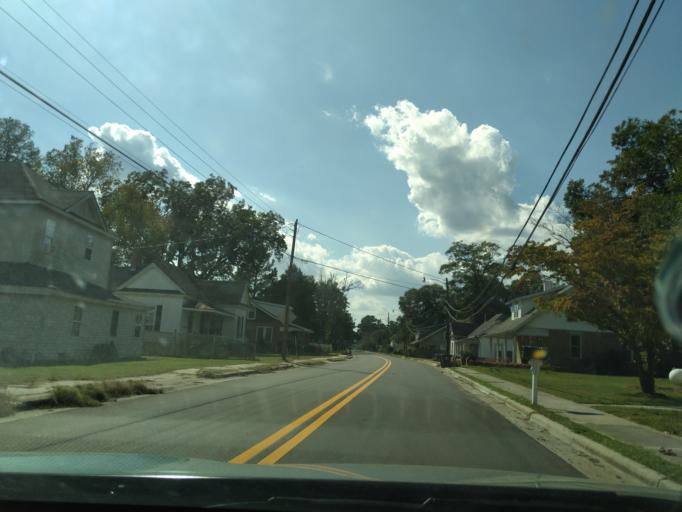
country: US
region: North Carolina
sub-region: Pitt County
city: Bethel
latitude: 35.8068
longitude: -77.3763
